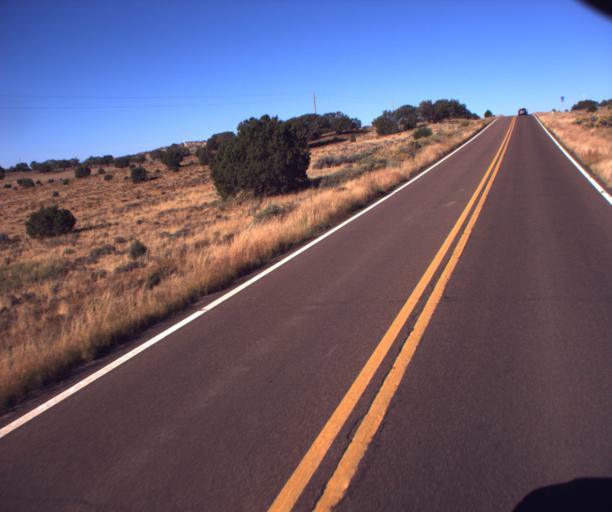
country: US
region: Arizona
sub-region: Apache County
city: Ganado
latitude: 35.7520
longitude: -109.8865
